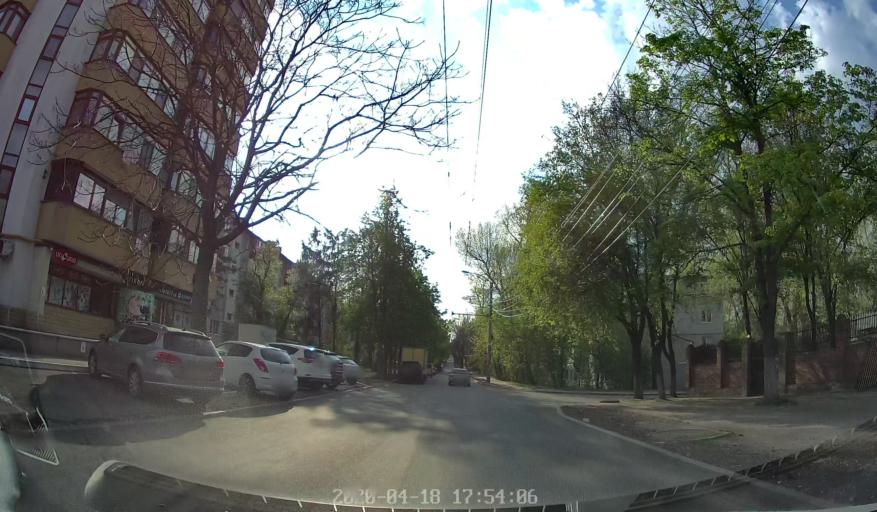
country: MD
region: Chisinau
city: Chisinau
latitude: 46.9932
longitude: 28.8537
